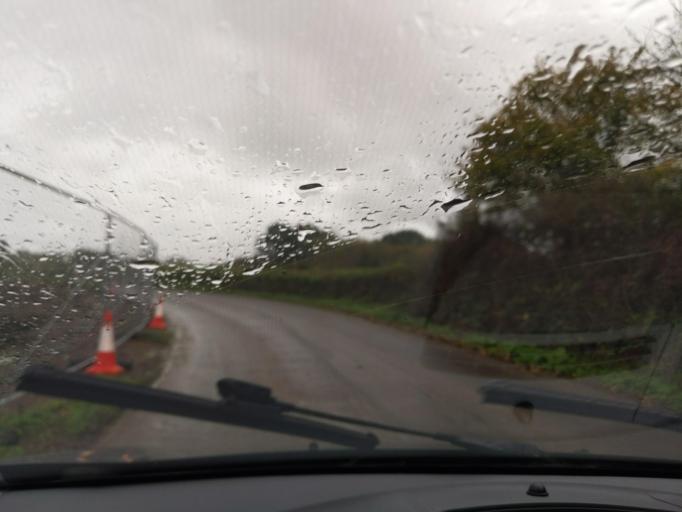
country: GB
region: England
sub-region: Cornwall
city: Wadebridge
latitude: 50.5176
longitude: -4.8200
